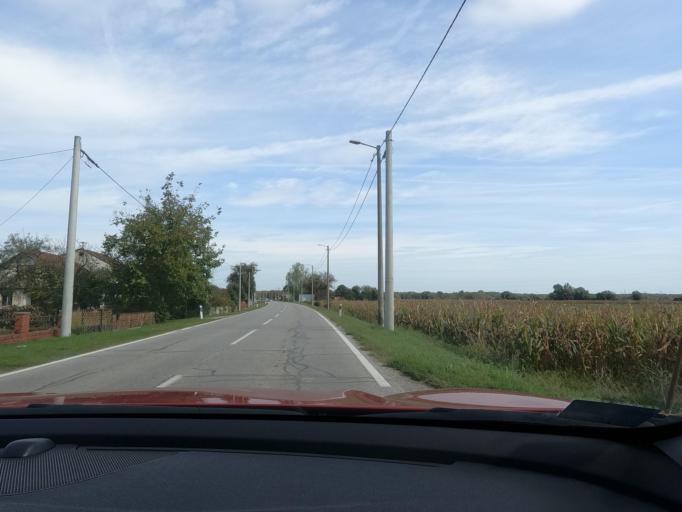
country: HR
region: Sisacko-Moslavacka
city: Budasevo
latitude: 45.4850
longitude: 16.4392
